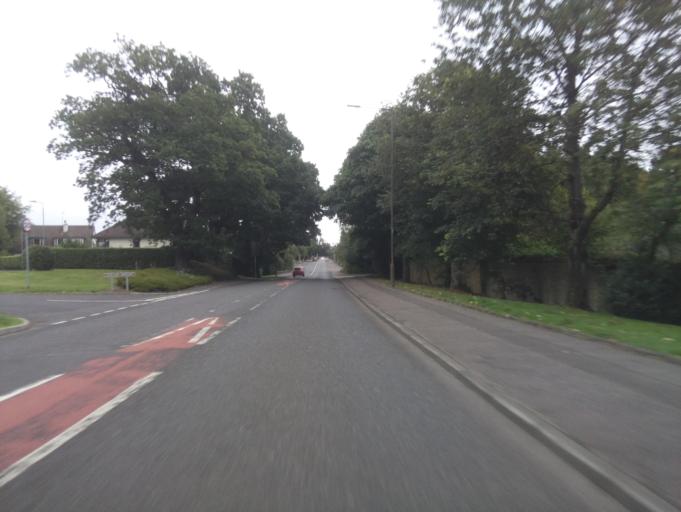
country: GB
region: Scotland
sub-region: Clackmannanshire
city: Dollar
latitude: 56.1632
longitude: -3.6848
